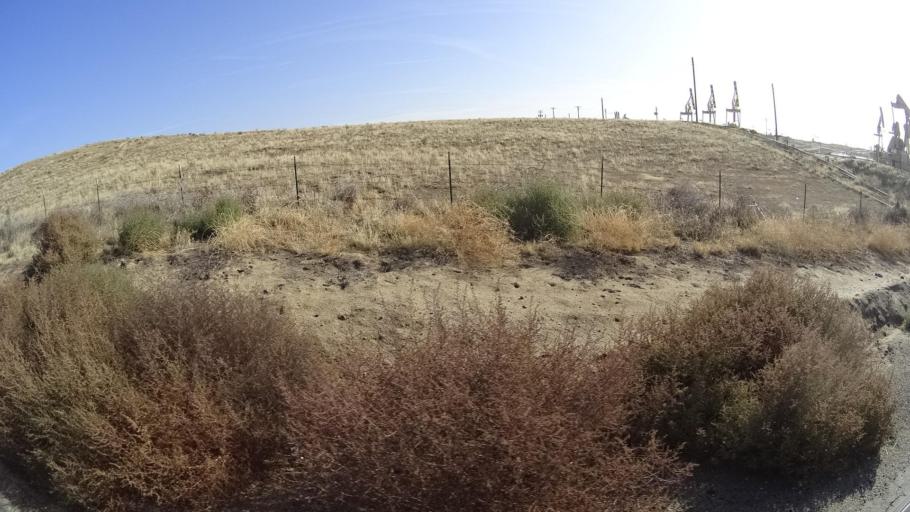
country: US
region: California
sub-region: Kern County
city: Oildale
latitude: 35.4794
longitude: -119.0460
